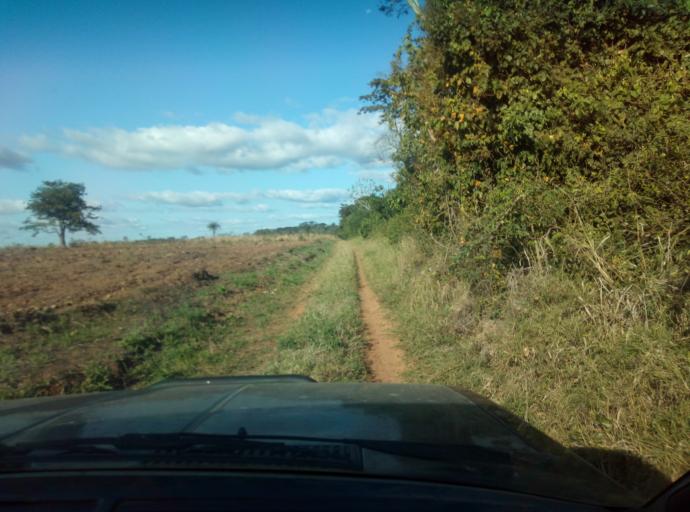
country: PY
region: Caaguazu
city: Carayao
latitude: -25.1734
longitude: -56.2798
